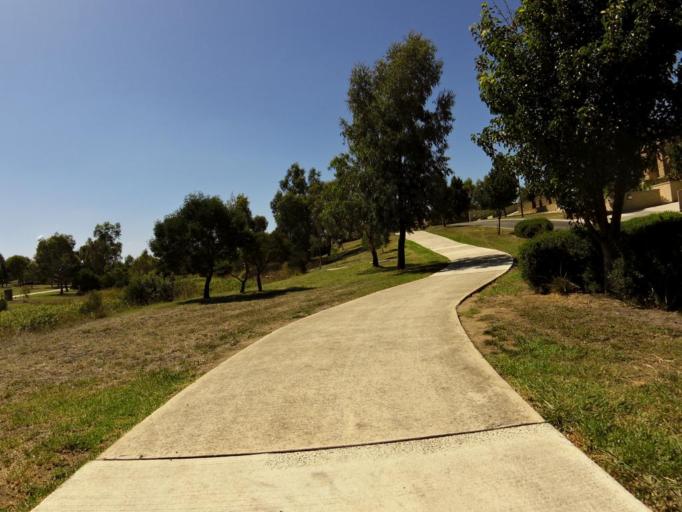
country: AU
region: Victoria
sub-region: Hume
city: Meadow Heights
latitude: -37.6490
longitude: 144.9070
